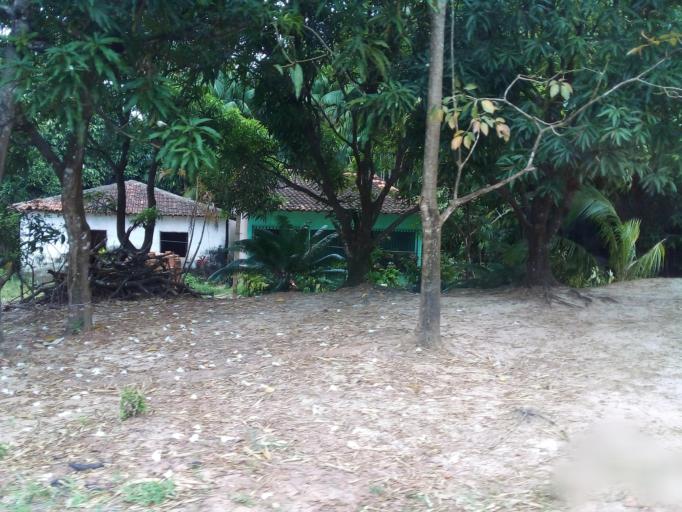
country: BR
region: Maranhao
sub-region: Sao Luis
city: Sao Luis
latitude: -2.6999
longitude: -44.3102
